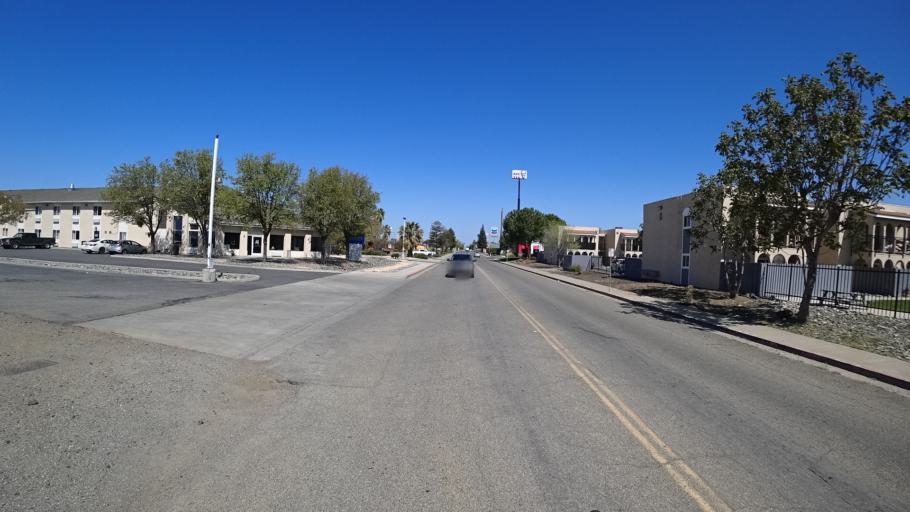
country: US
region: California
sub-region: Glenn County
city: Willows
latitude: 39.5211
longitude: -122.2122
